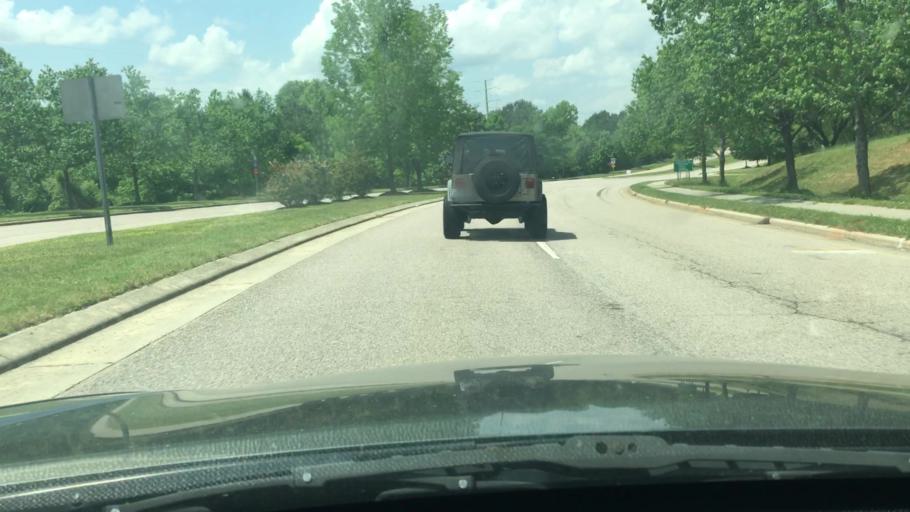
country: US
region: North Carolina
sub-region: Wake County
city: West Raleigh
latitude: 35.7614
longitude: -78.6651
